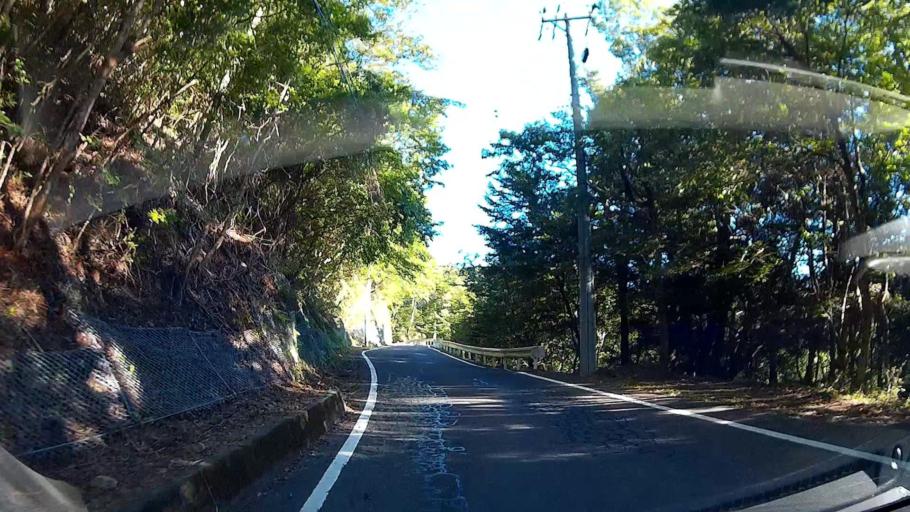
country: JP
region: Shizuoka
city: Shizuoka-shi
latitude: 35.2005
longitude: 138.2524
